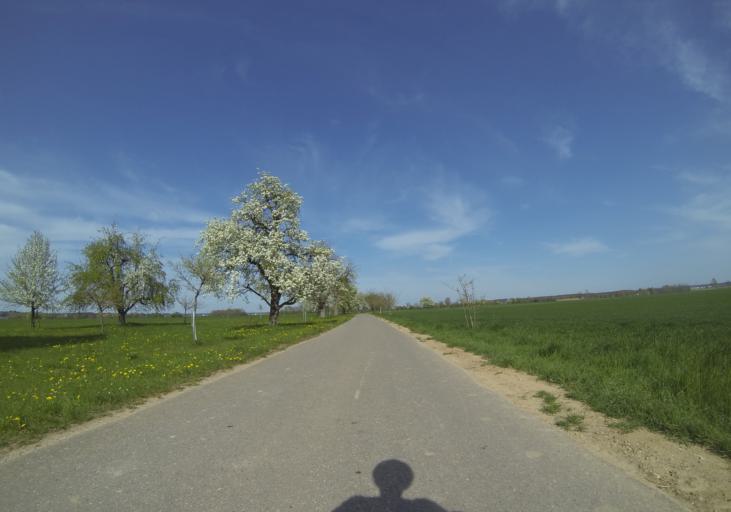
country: DE
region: Baden-Wuerttemberg
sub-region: Tuebingen Region
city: Huttisheim
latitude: 48.2832
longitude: 9.9523
